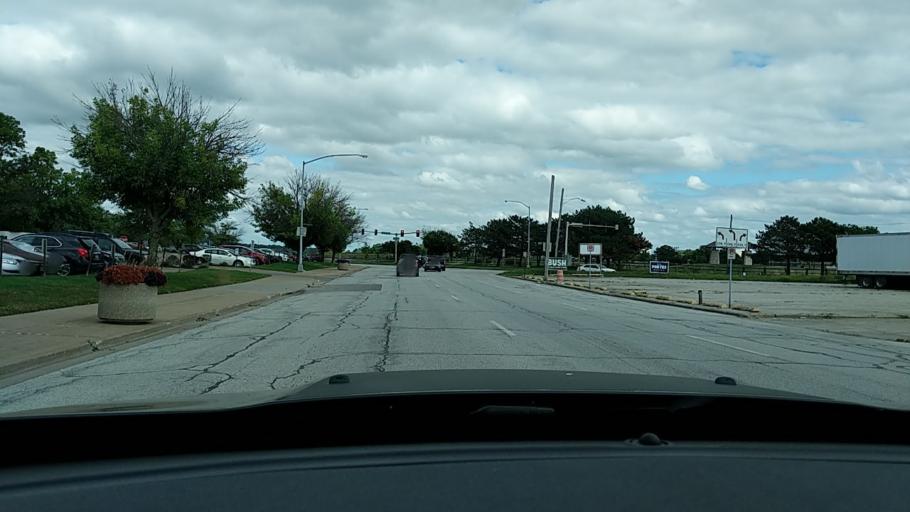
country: US
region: Iowa
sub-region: Scott County
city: Davenport
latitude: 41.5224
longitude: -90.5674
